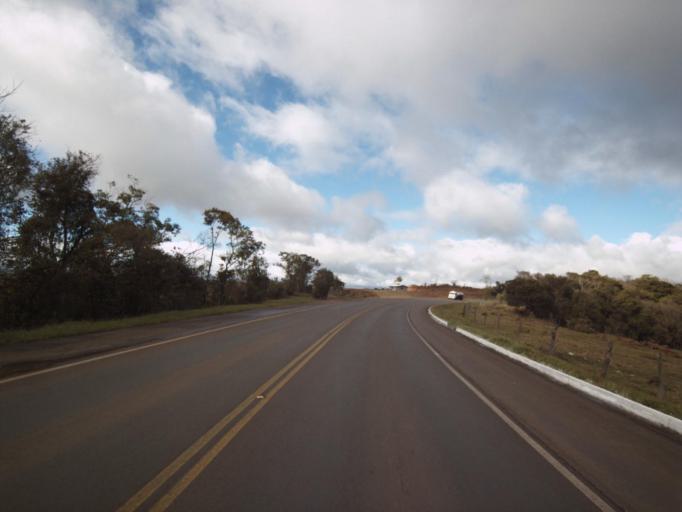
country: BR
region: Santa Catarina
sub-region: Concordia
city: Concordia
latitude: -27.1056
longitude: -51.9003
